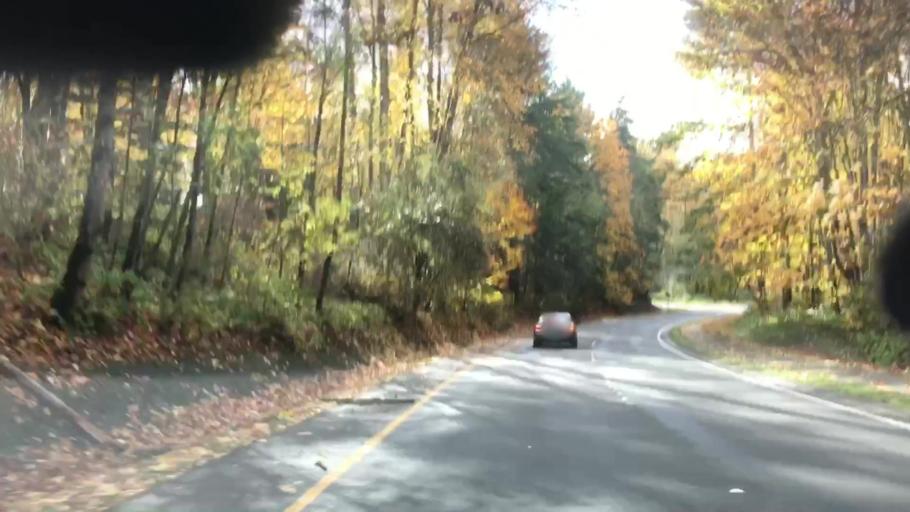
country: US
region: Washington
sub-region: King County
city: Eastgate
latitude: 47.5989
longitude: -122.1606
